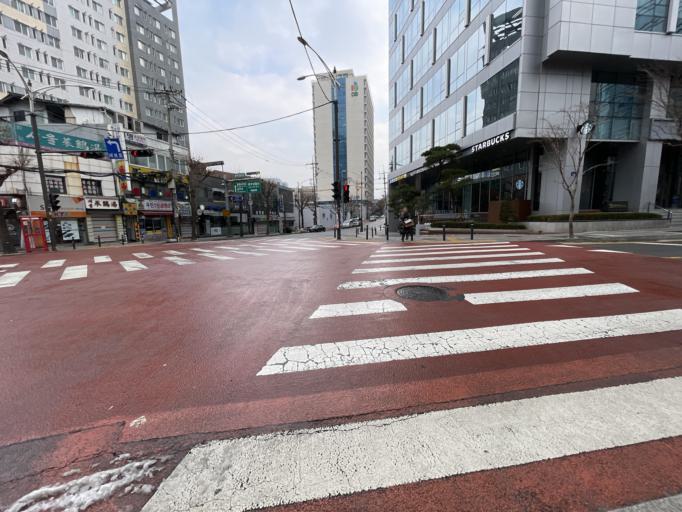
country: KR
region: Seoul
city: Seoul
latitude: 37.5648
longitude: 126.9899
